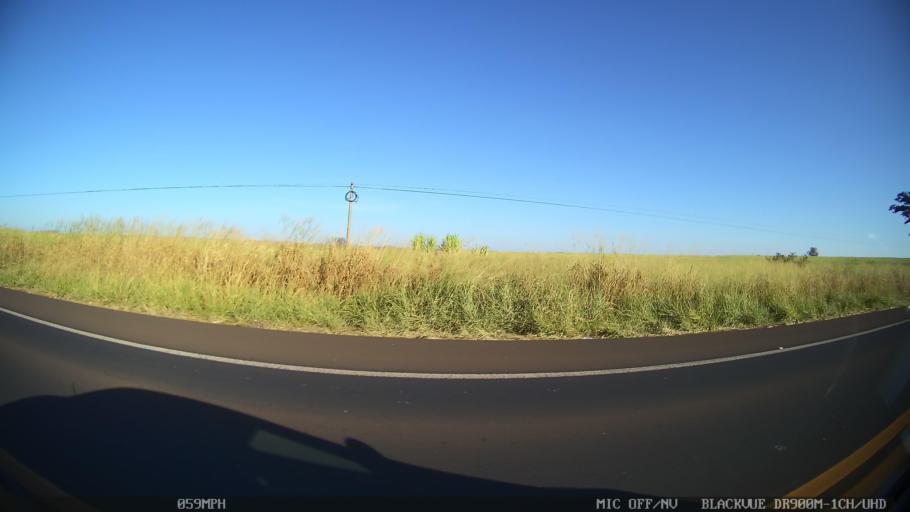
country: BR
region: Sao Paulo
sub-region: Olimpia
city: Olimpia
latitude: -20.7254
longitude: -49.0343
